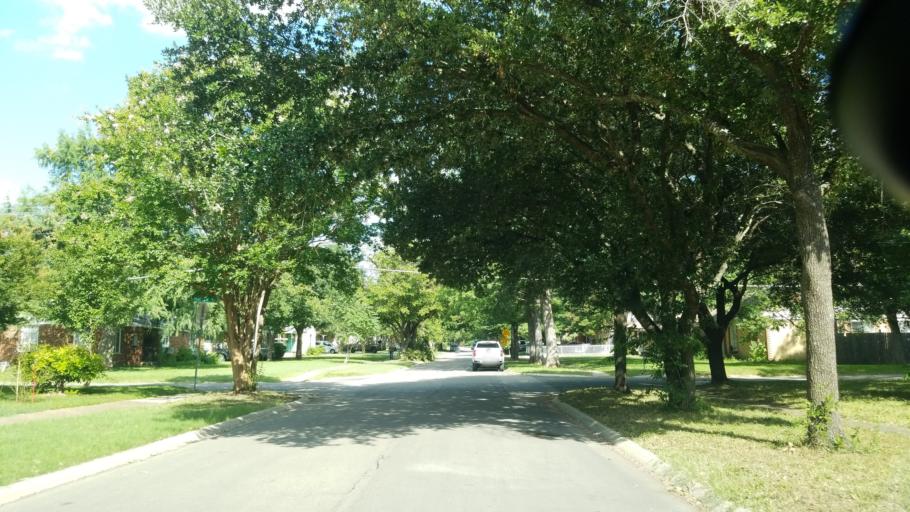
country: US
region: Texas
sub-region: Dallas County
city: Dallas
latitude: 32.7731
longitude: -96.7158
